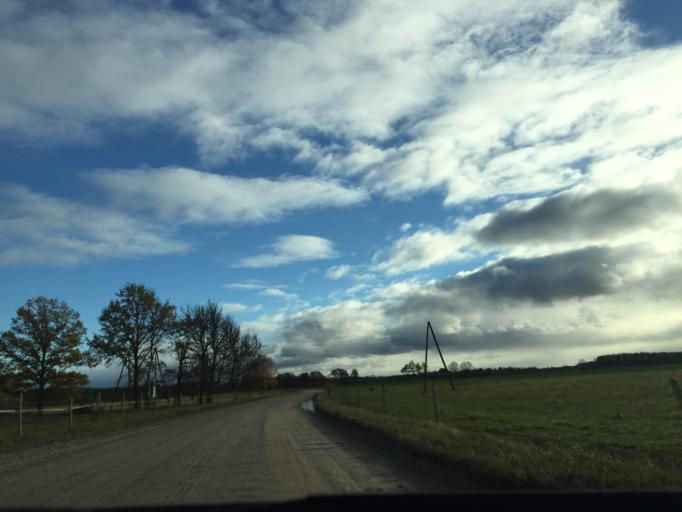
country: LV
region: Kandava
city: Kandava
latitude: 56.9418
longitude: 22.9502
